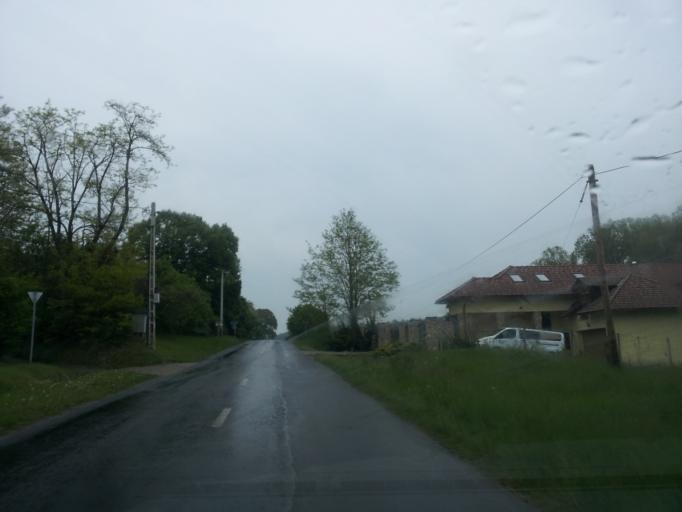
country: HU
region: Tolna
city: Szekszard
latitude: 46.2826
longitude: 18.6458
